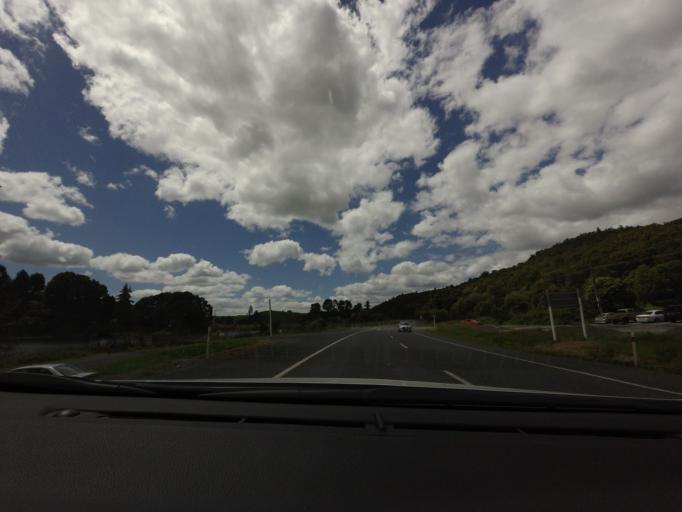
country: NZ
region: Bay of Plenty
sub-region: Rotorua District
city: Rotorua
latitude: -38.3154
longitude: 176.3754
